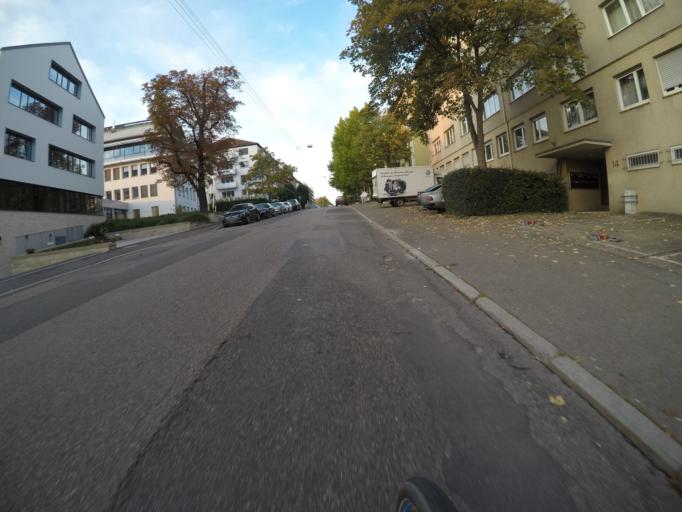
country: DE
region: Baden-Wuerttemberg
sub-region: Regierungsbezirk Stuttgart
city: Stuttgart
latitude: 48.7785
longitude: 9.1889
